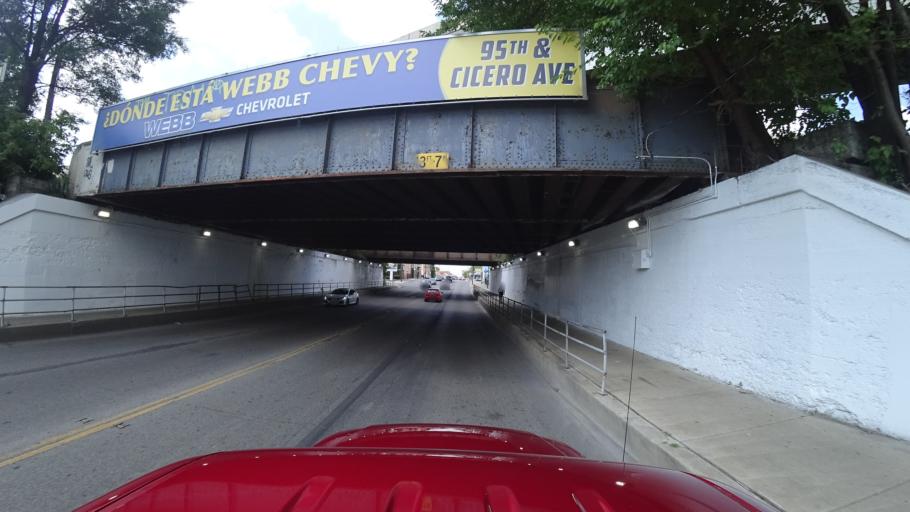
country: US
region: Illinois
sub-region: Cook County
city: Chicago
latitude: 41.8254
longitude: -87.6859
